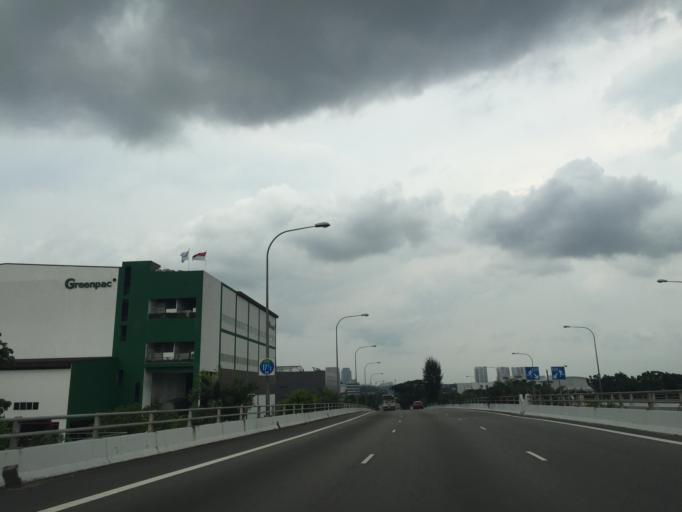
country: SG
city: Singapore
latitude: 1.3217
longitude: 103.7108
